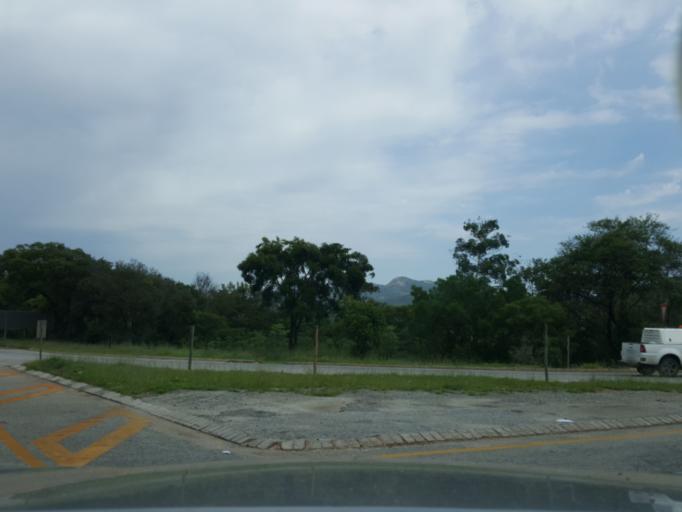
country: ZA
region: Mpumalanga
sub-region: Ehlanzeni District
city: Nelspruit
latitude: -25.4727
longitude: 31.0928
